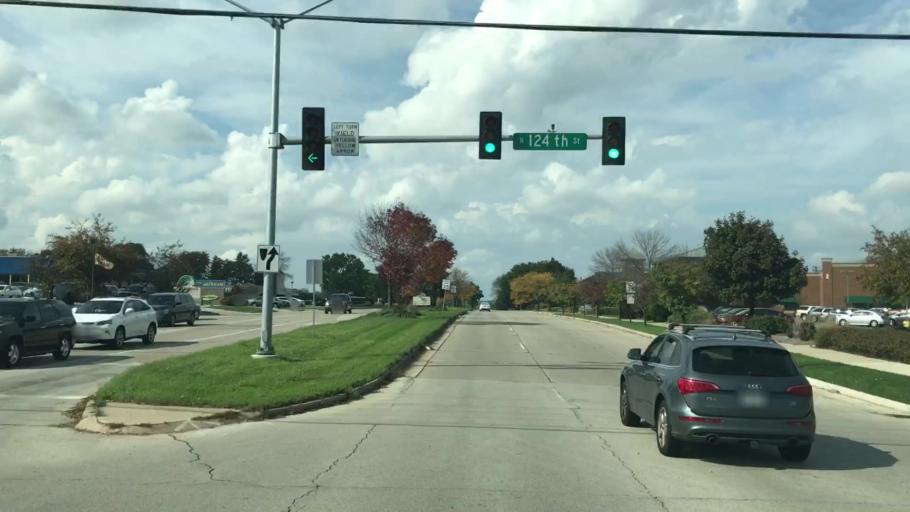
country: US
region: Wisconsin
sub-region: Waukesha County
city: Elm Grove
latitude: 43.0600
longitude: -88.0670
